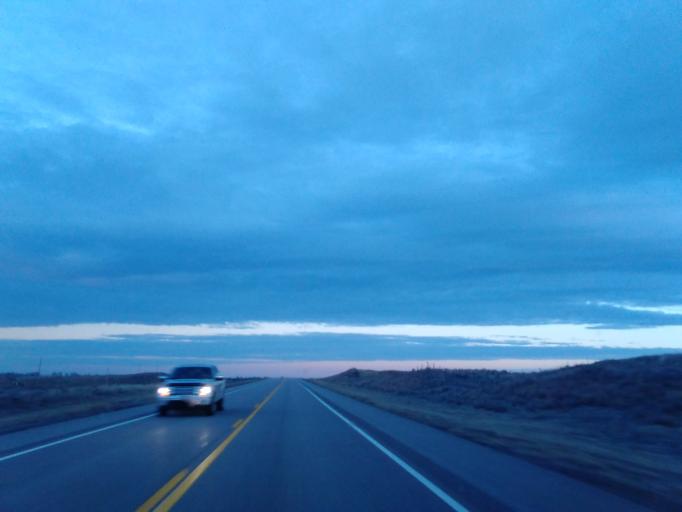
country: US
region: Nebraska
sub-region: Garden County
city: Oshkosh
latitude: 41.3745
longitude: -102.2544
